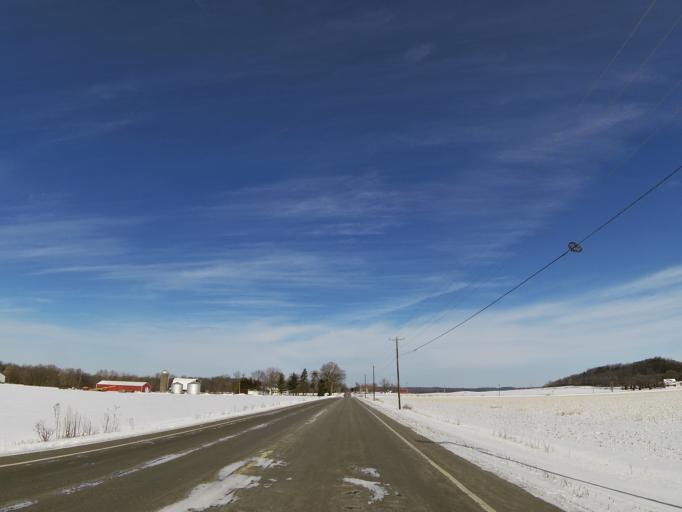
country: US
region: Minnesota
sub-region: Washington County
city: Afton
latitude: 44.8414
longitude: -92.7311
